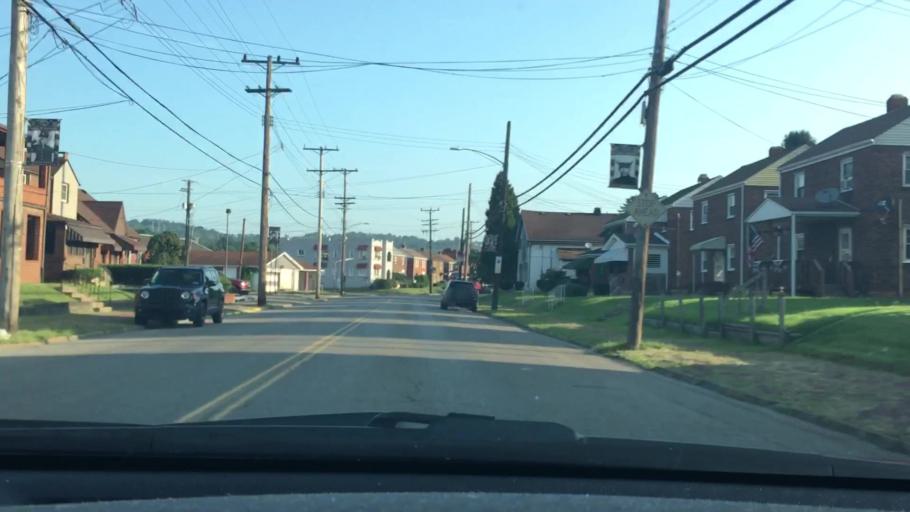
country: US
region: Pennsylvania
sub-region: Allegheny County
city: Glassport
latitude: 40.3299
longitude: -79.8925
